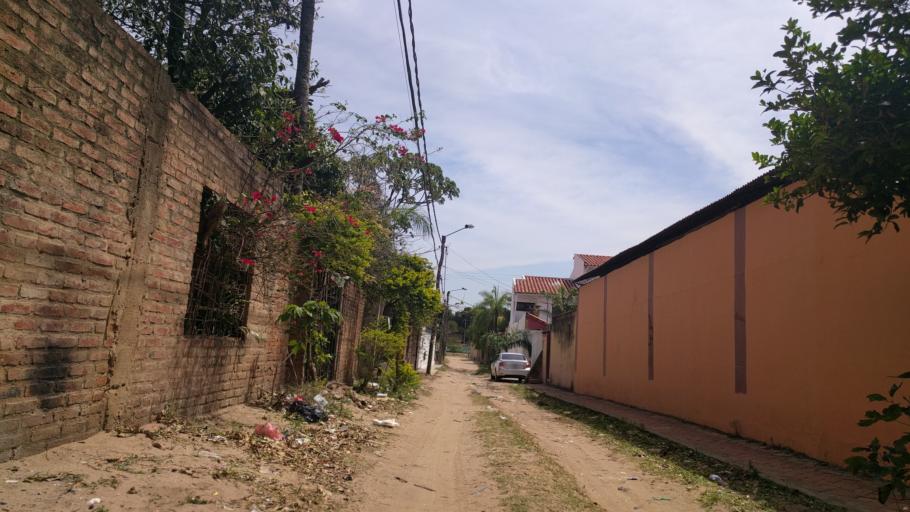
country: BO
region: Santa Cruz
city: Santa Cruz de la Sierra
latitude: -17.8142
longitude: -63.2199
